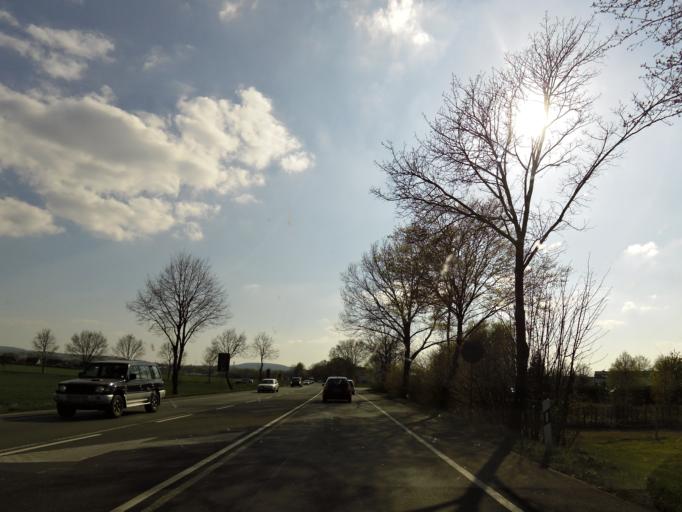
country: DE
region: North Rhine-Westphalia
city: Porta Westfalica
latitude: 52.2246
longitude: 8.8837
